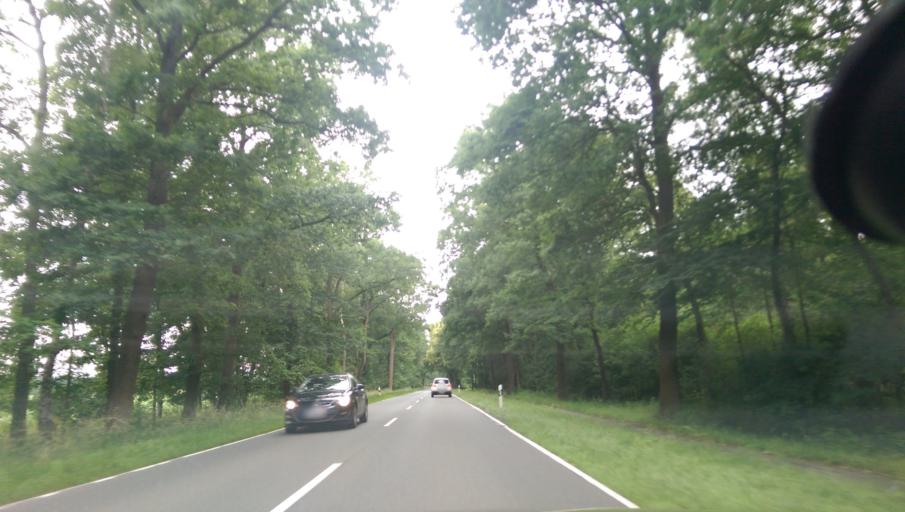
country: DE
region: Lower Saxony
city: Hemsbunde
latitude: 53.0722
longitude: 9.4388
